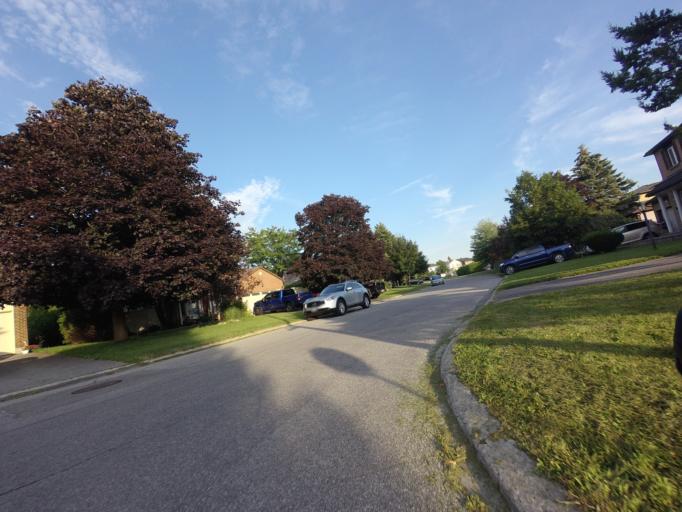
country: CA
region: Ontario
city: Bells Corners
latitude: 45.2784
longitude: -75.7737
